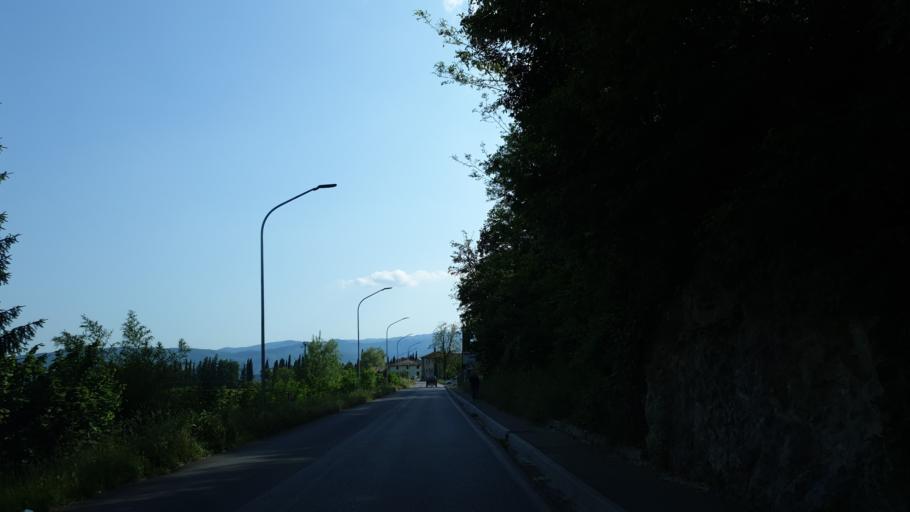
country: IT
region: Tuscany
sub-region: Province of Arezzo
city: Soci
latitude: 43.7478
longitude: 11.8200
